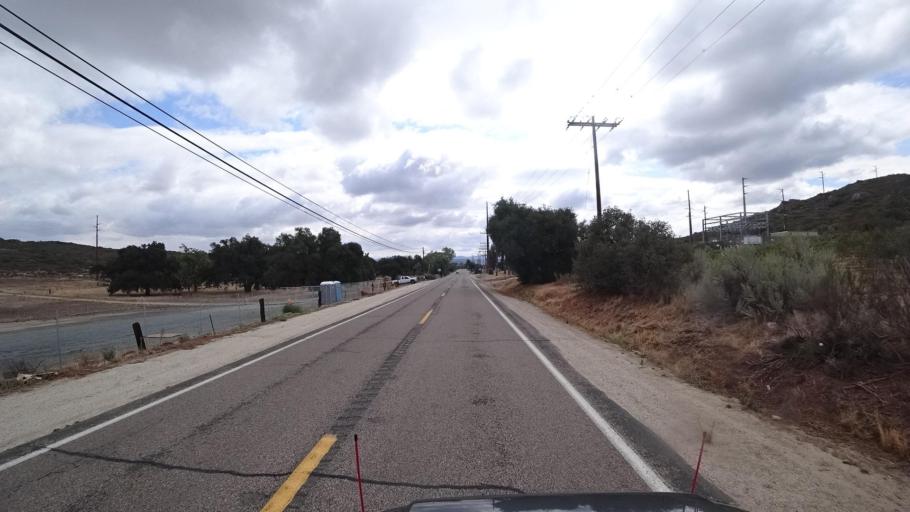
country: US
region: California
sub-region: San Diego County
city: Campo
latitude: 32.6542
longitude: -116.4876
